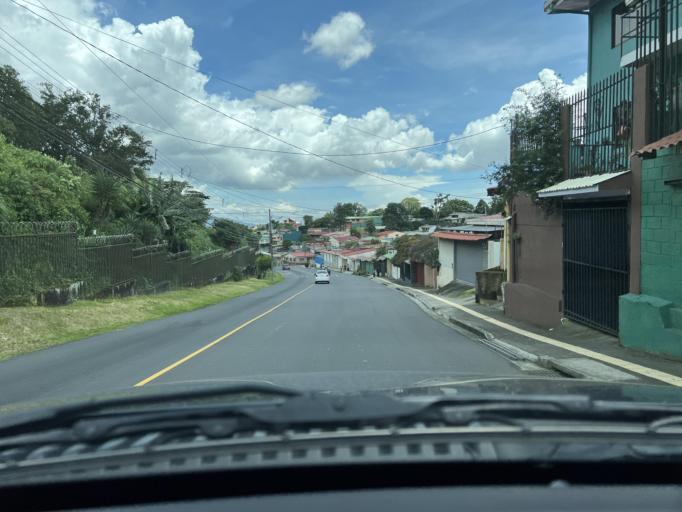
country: CR
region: San Jose
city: Granadilla
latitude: 9.9432
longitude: -84.0244
